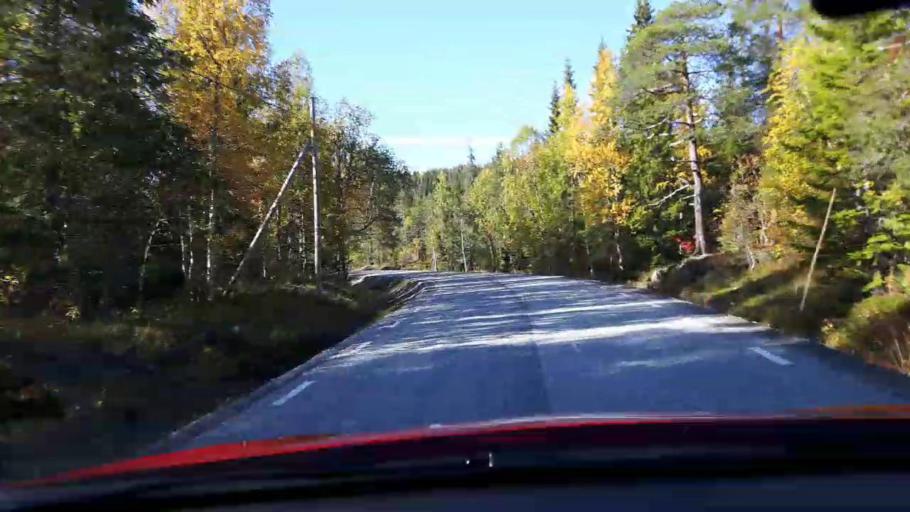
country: NO
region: Nord-Trondelag
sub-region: Royrvik
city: Royrvik
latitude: 64.8189
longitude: 14.2299
